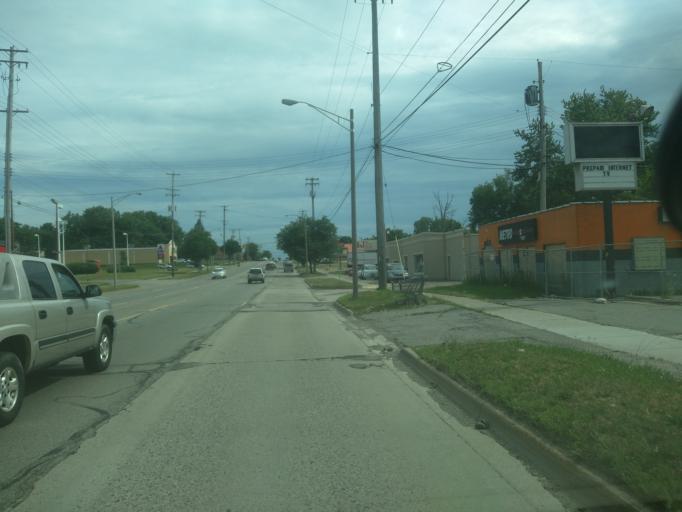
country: US
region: Michigan
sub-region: Ingham County
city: Lansing
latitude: 42.6927
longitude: -84.5676
